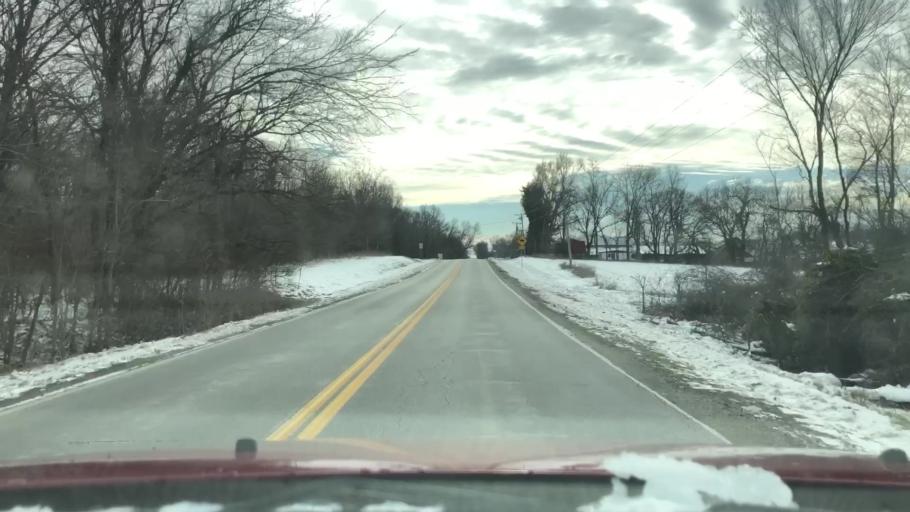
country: US
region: Missouri
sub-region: Jackson County
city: Greenwood
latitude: 38.8819
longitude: -94.3409
